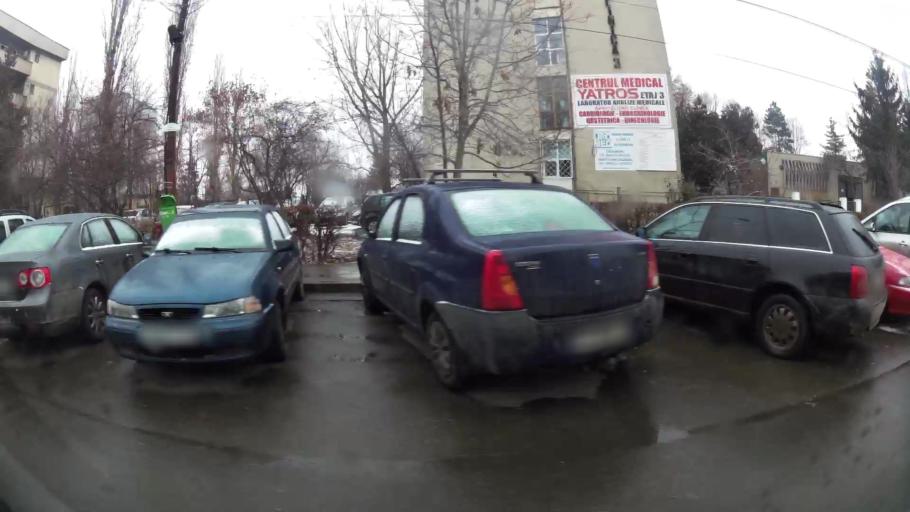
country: RO
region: Prahova
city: Ploiesti
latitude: 44.9525
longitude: 26.0112
